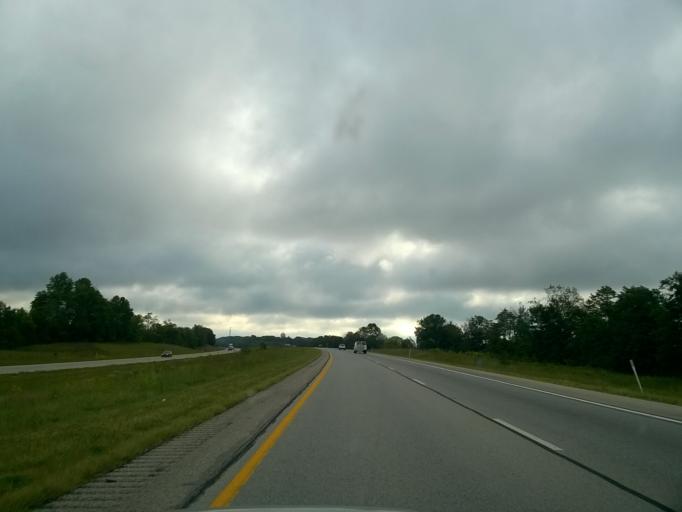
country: US
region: Indiana
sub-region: Harrison County
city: Corydon
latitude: 38.2467
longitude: -86.0711
